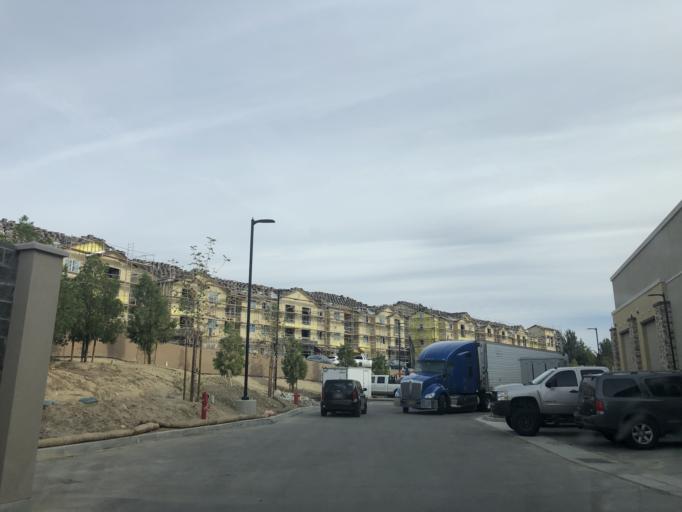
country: US
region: California
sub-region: Los Angeles County
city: Chatsworth
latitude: 34.2773
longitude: -118.5729
